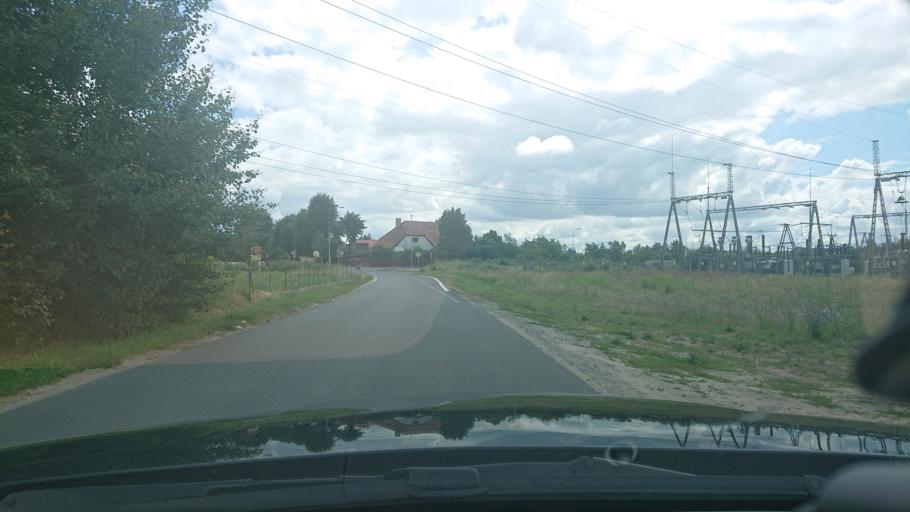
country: PL
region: Greater Poland Voivodeship
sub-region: Powiat gnieznienski
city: Gniezno
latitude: 52.5170
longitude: 17.6219
